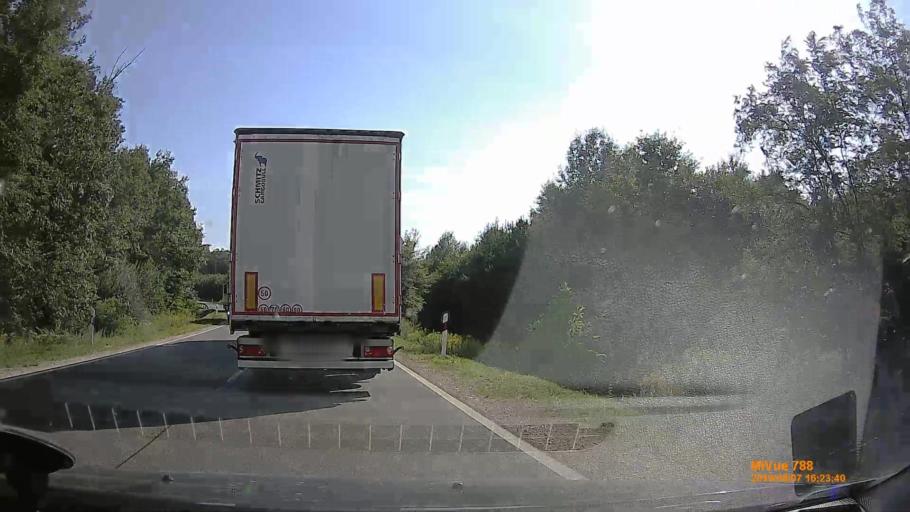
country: HU
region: Zala
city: Zalalovo
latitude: 46.7453
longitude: 16.5551
